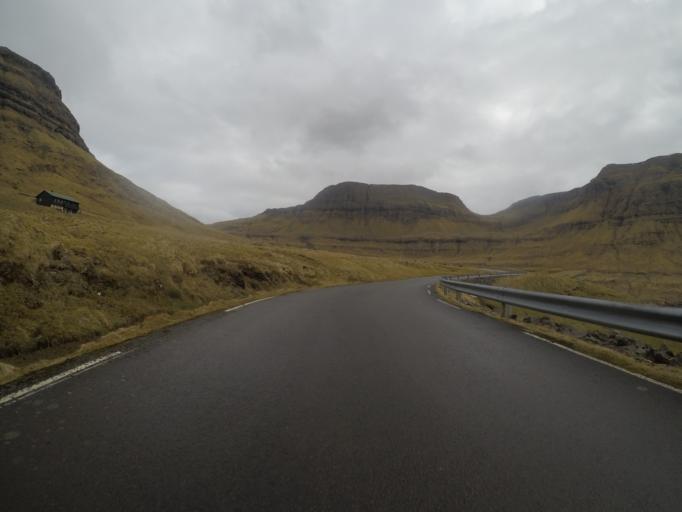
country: FO
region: Streymoy
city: Kollafjordhur
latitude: 62.0416
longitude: -6.9399
